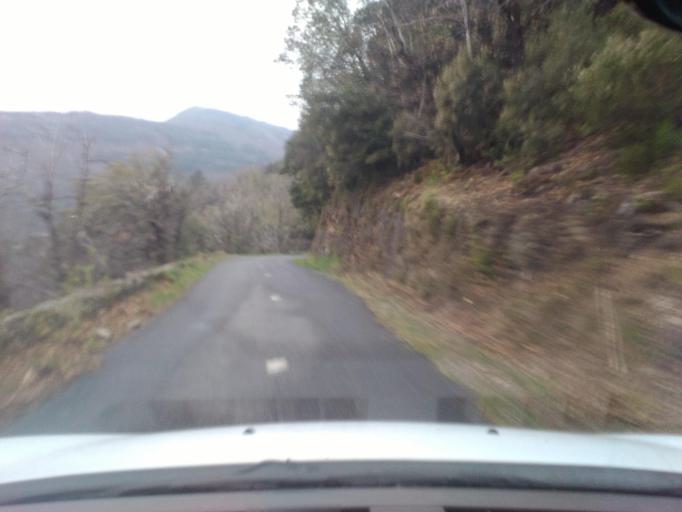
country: FR
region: Languedoc-Roussillon
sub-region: Departement du Gard
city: Valleraugue
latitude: 44.1008
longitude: 3.6406
